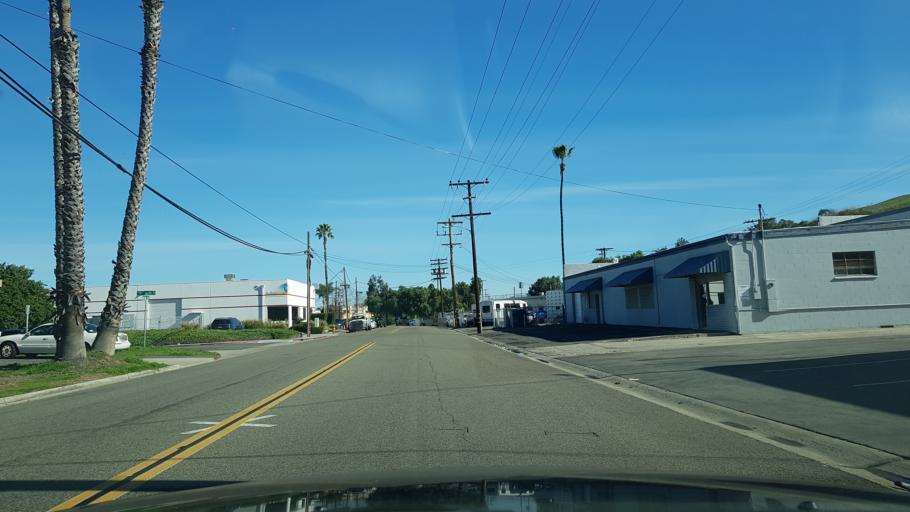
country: US
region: California
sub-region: San Diego County
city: Oceanside
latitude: 33.2105
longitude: -117.3523
